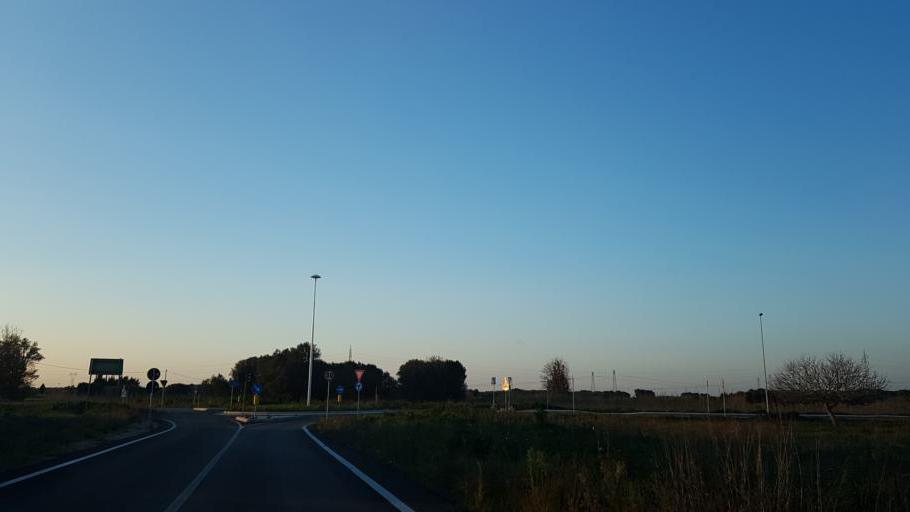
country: IT
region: Apulia
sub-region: Provincia di Brindisi
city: Tuturano
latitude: 40.5455
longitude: 17.9424
